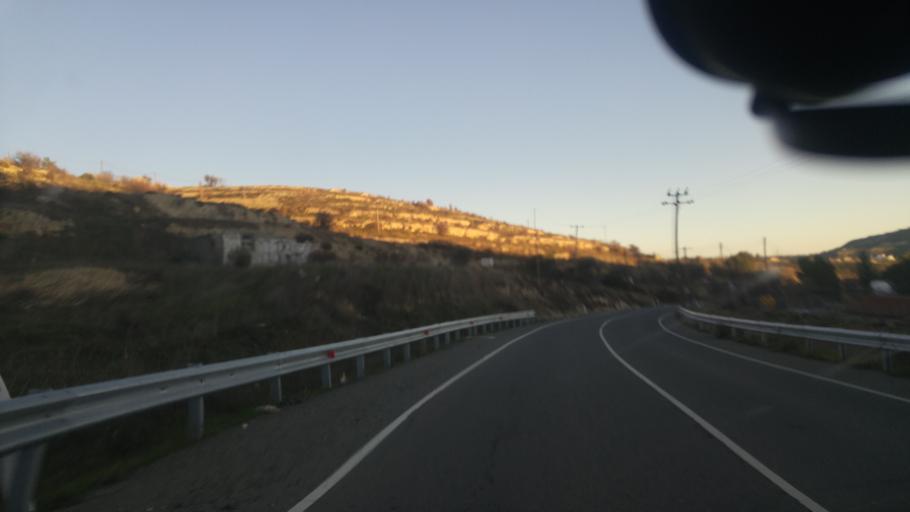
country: CY
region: Limassol
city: Pachna
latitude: 34.7940
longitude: 32.8205
